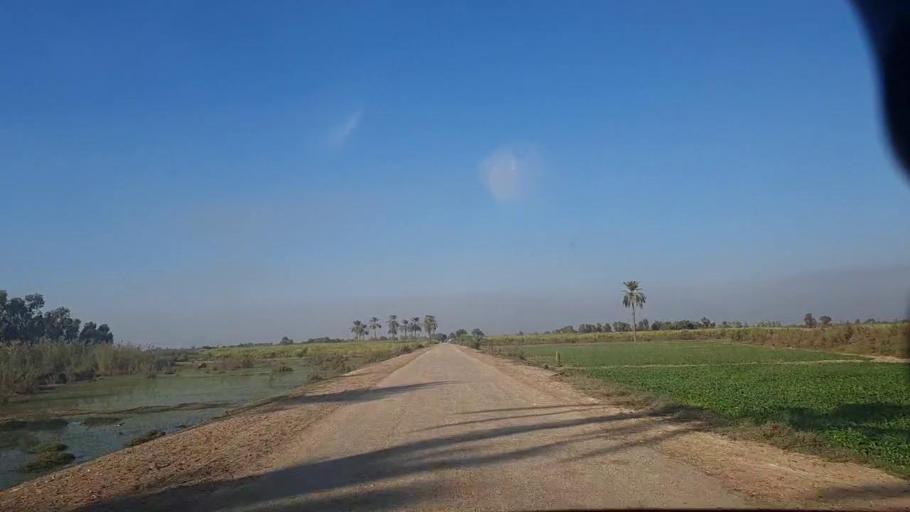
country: PK
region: Sindh
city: Sobhadero
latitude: 27.4082
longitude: 68.4222
